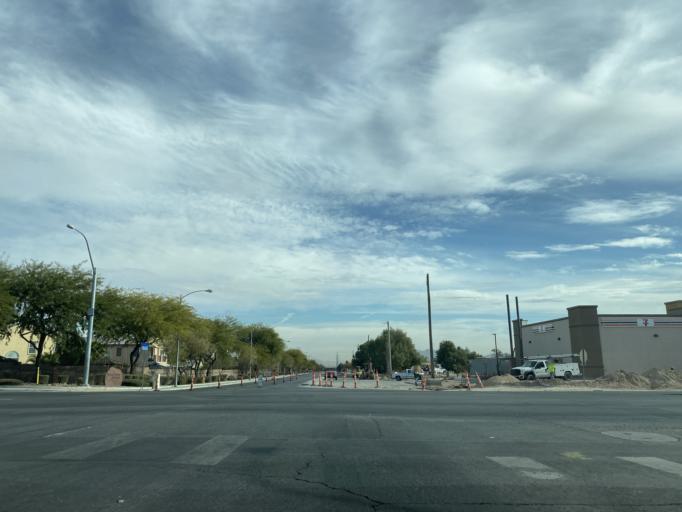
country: US
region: Nevada
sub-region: Clark County
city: North Las Vegas
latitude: 36.2469
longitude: -115.1352
